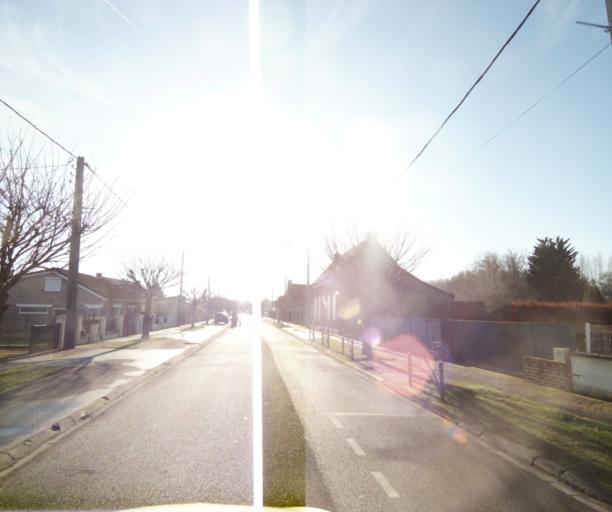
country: FR
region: Nord-Pas-de-Calais
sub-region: Departement du Nord
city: Trith-Saint-Leger
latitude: 50.3132
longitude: 3.4843
